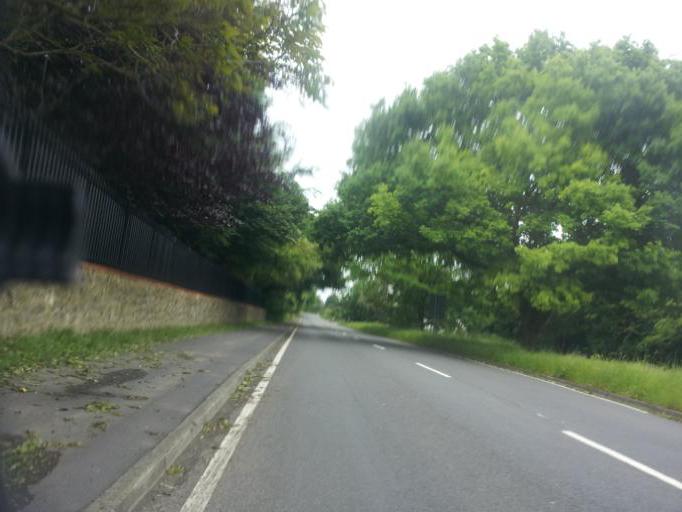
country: GB
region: England
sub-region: Kent
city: Wateringbury
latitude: 51.2544
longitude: 0.4628
